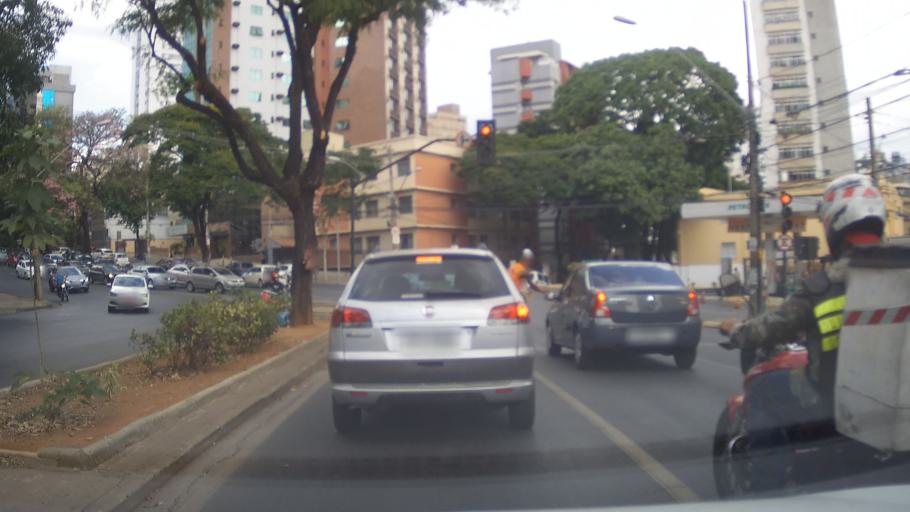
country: BR
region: Minas Gerais
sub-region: Belo Horizonte
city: Belo Horizonte
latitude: -19.9383
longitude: -43.9442
